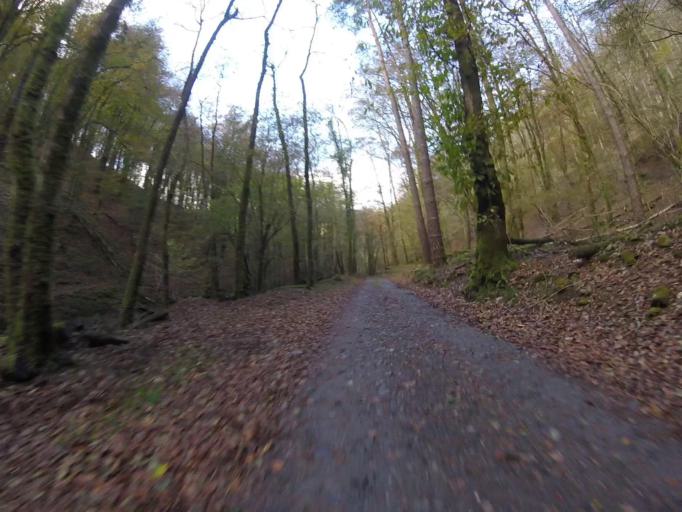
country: ES
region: Navarre
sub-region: Provincia de Navarra
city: Goizueta
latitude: 43.2042
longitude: -1.8084
